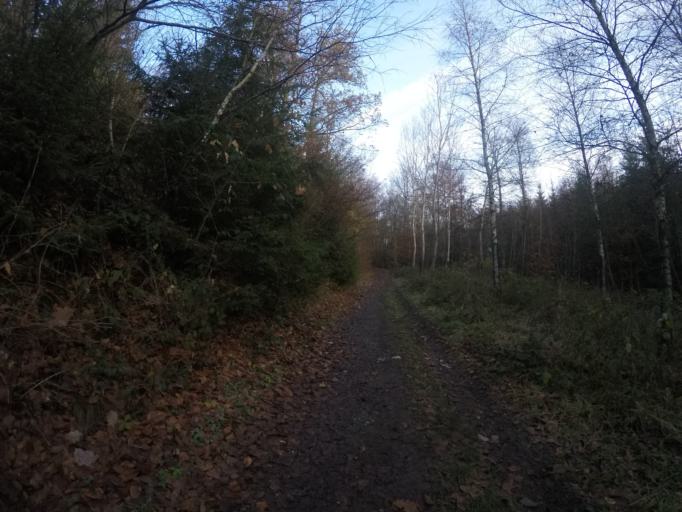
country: BE
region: Wallonia
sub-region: Province du Luxembourg
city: Habay-la-Vieille
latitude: 49.7331
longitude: 5.6592
